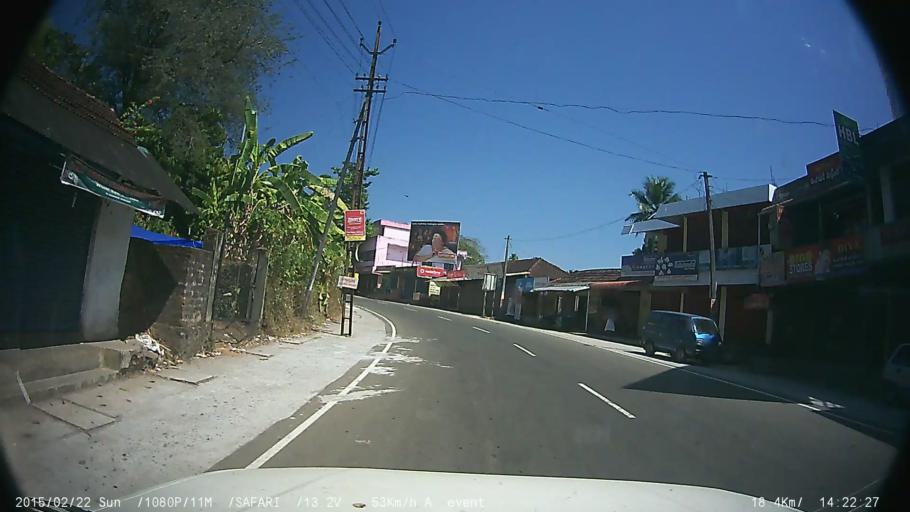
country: IN
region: Kerala
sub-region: Kottayam
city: Lalam
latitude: 9.5665
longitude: 76.7069
